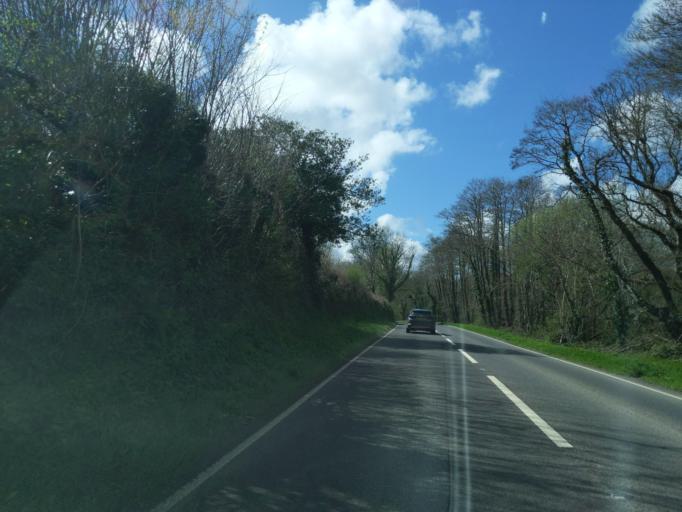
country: GB
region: England
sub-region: Cornwall
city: Wadebridge
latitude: 50.5081
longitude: -4.7968
